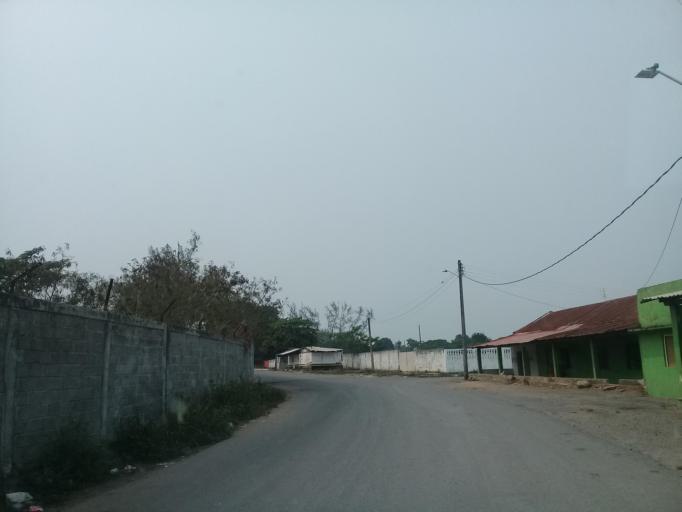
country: MX
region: Veracruz
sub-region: Medellin
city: La Laguna y Monte del Castillo
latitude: 18.9694
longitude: -96.1194
